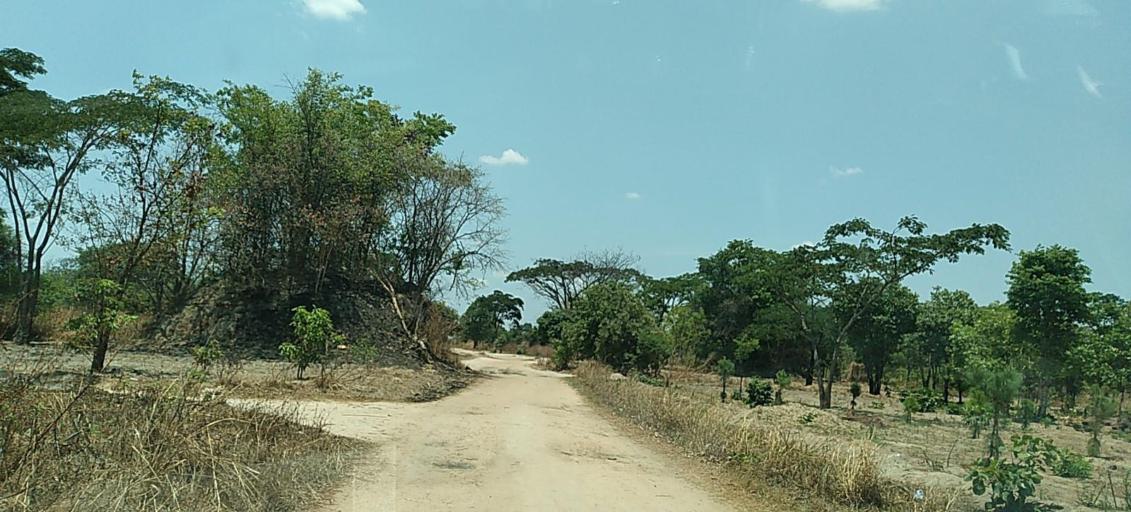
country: ZM
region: Copperbelt
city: Luanshya
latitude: -13.0794
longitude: 28.4052
